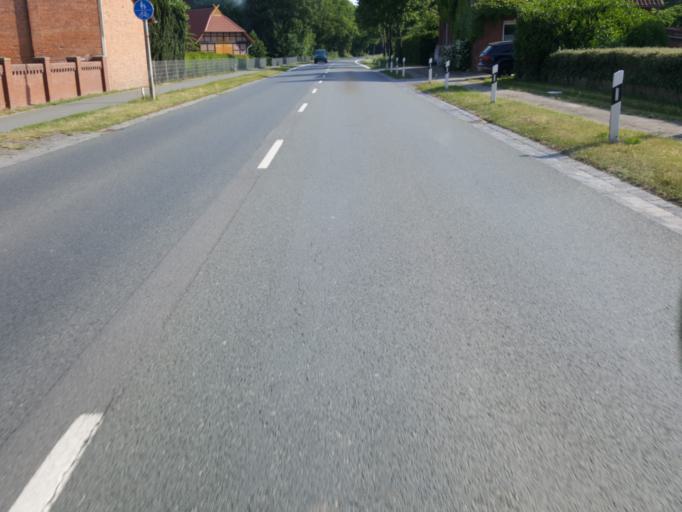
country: DE
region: Lower Saxony
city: Estorf
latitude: 52.5894
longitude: 9.1424
